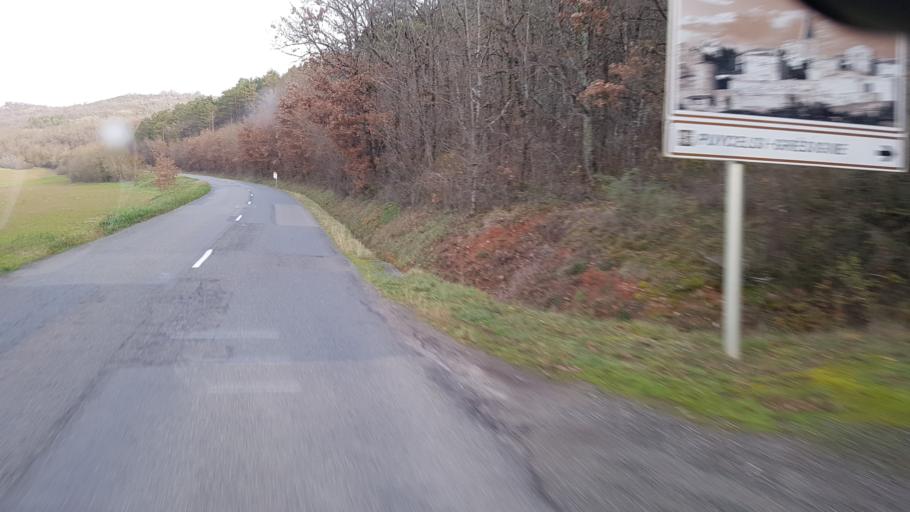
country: FR
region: Midi-Pyrenees
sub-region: Departement du Tarn-et-Garonne
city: Monclar-de-Quercy
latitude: 43.9740
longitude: 1.7285
